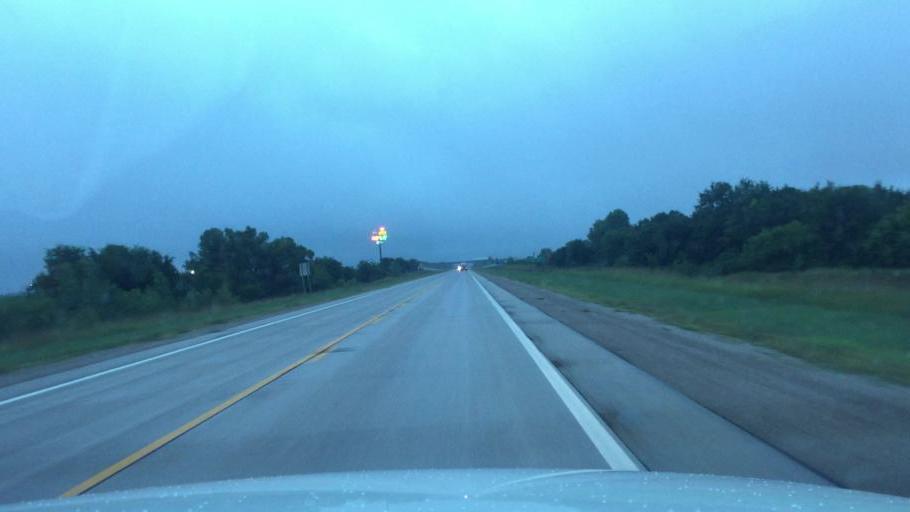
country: US
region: Kansas
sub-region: Neosho County
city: Chanute
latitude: 37.6550
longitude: -95.4797
